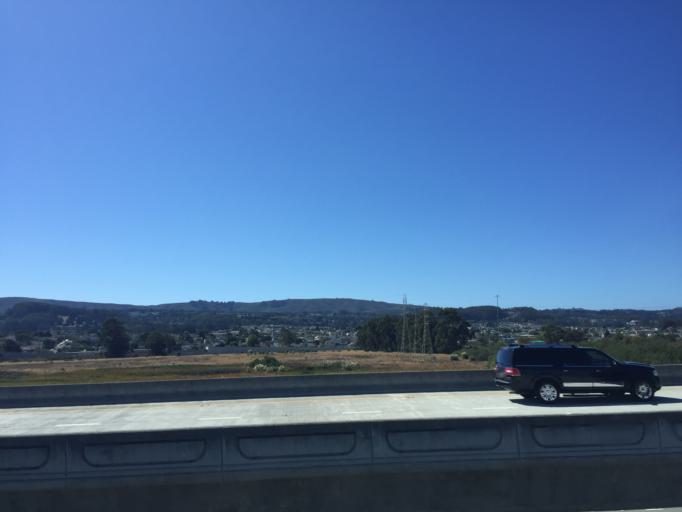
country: US
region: California
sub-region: San Mateo County
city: San Bruno
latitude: 37.6228
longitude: -122.3999
